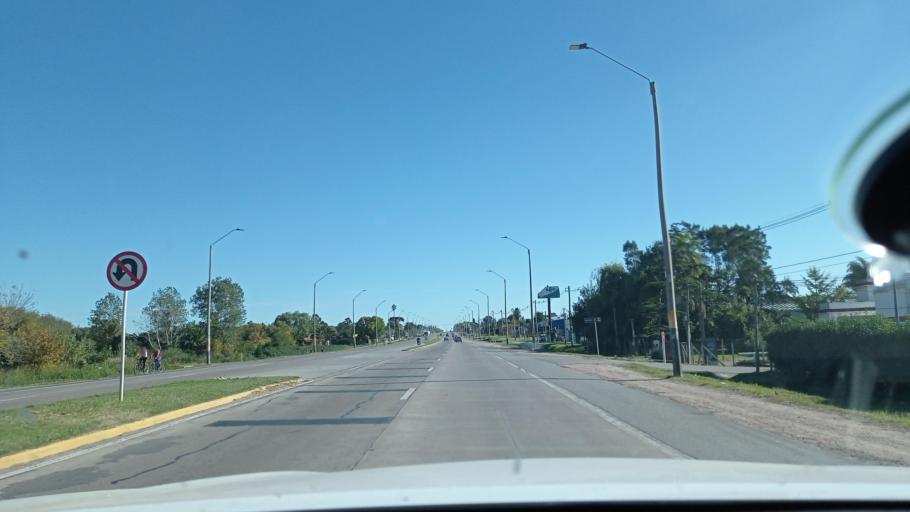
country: UY
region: Canelones
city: Joaquin Suarez
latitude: -34.7561
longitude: -56.0068
